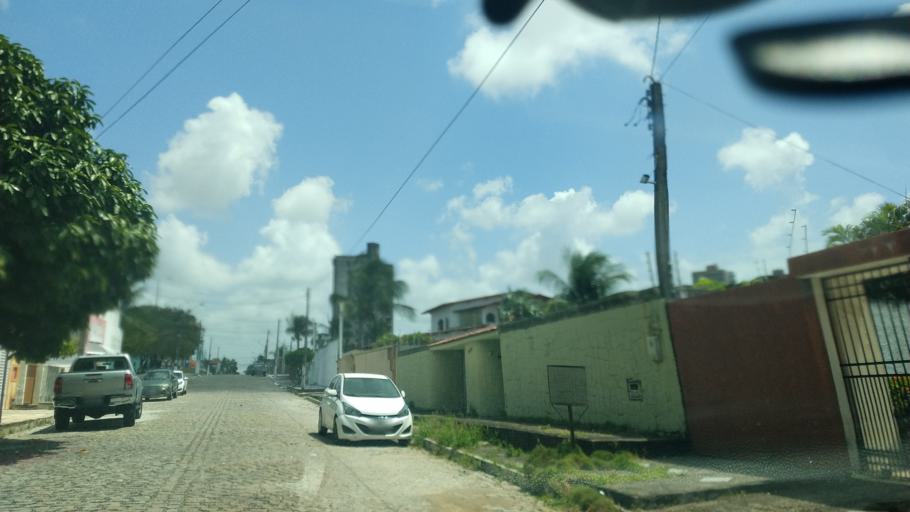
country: BR
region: Rio Grande do Norte
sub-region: Natal
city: Natal
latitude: -5.8635
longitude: -35.1962
